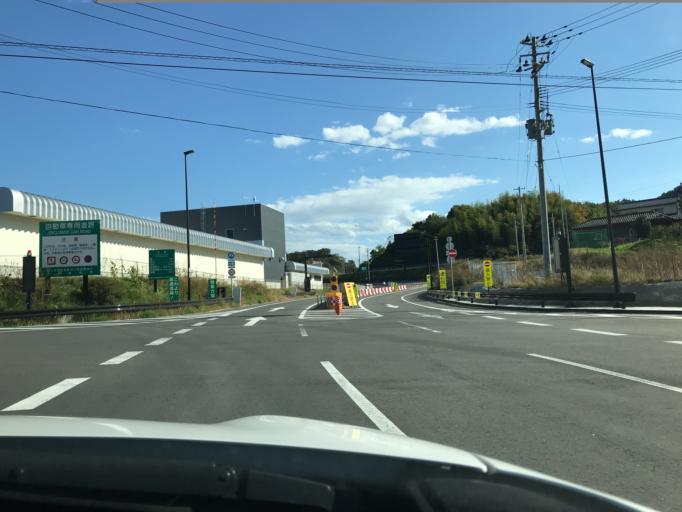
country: JP
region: Fukushima
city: Hobaramachi
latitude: 37.7664
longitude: 140.5883
